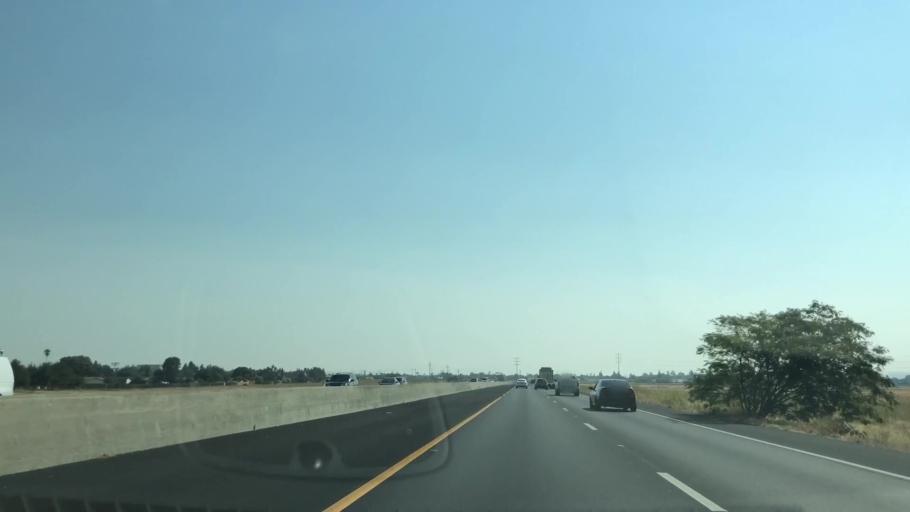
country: US
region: California
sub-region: Solano County
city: Suisun
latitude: 38.2405
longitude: -122.0612
